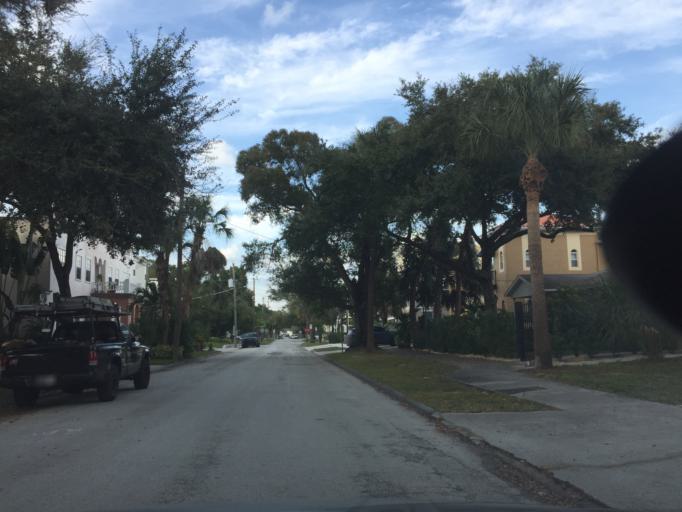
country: US
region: Florida
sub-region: Hillsborough County
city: Tampa
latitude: 27.9400
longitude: -82.4799
